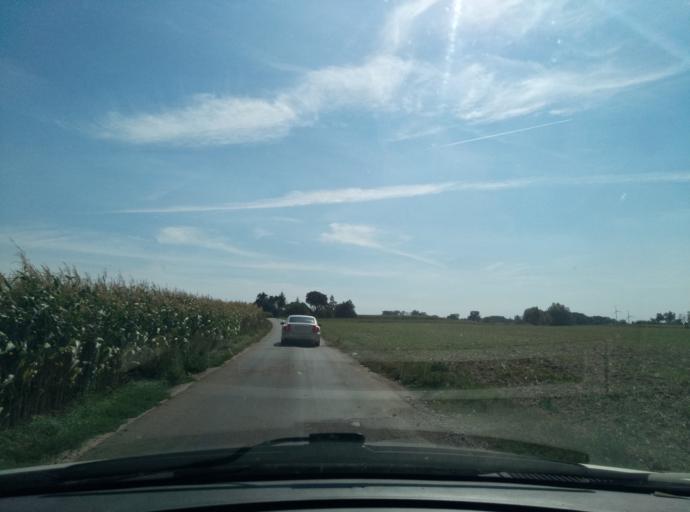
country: PL
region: Kujawsko-Pomorskie
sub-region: Powiat brodnicki
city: Jablonowo Pomorskie
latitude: 53.4062
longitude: 19.2384
